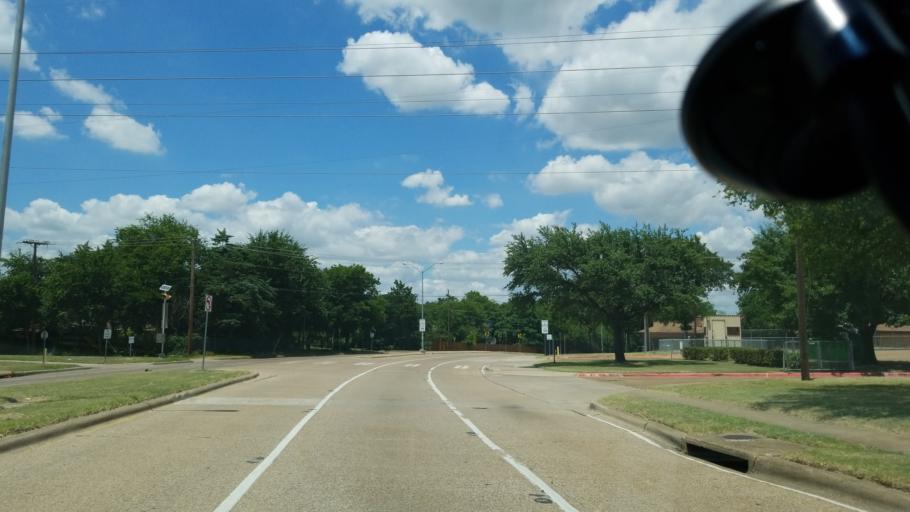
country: US
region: Texas
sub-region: Dallas County
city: Cockrell Hill
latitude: 32.7005
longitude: -96.8785
